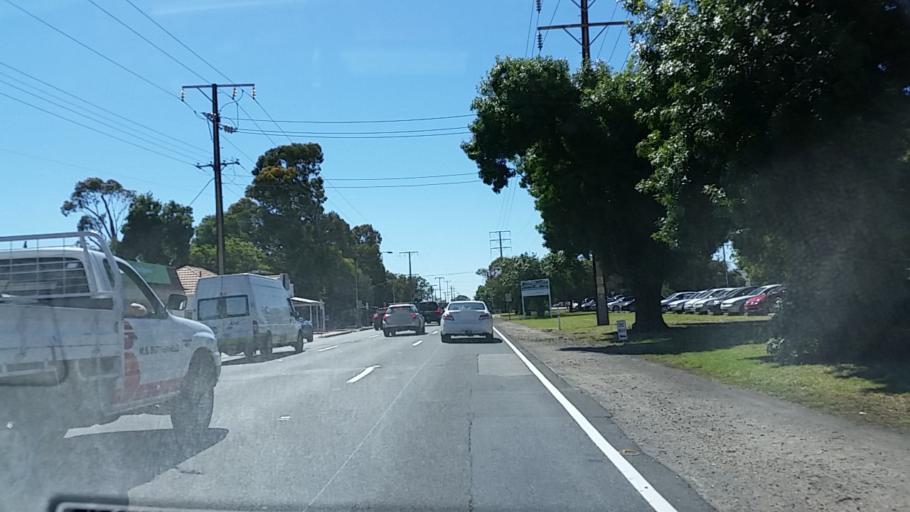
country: AU
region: South Australia
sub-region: Charles Sturt
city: Woodville West
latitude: -34.8802
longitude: 138.5339
